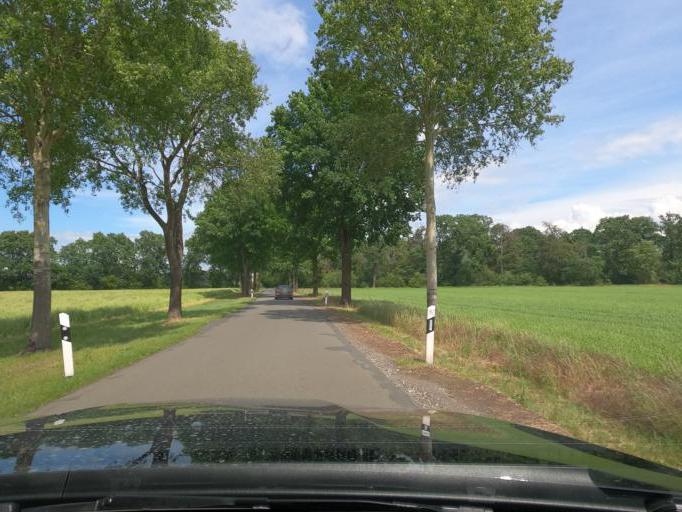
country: DE
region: Lower Saxony
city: Lindwedel
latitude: 52.6193
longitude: 9.6483
